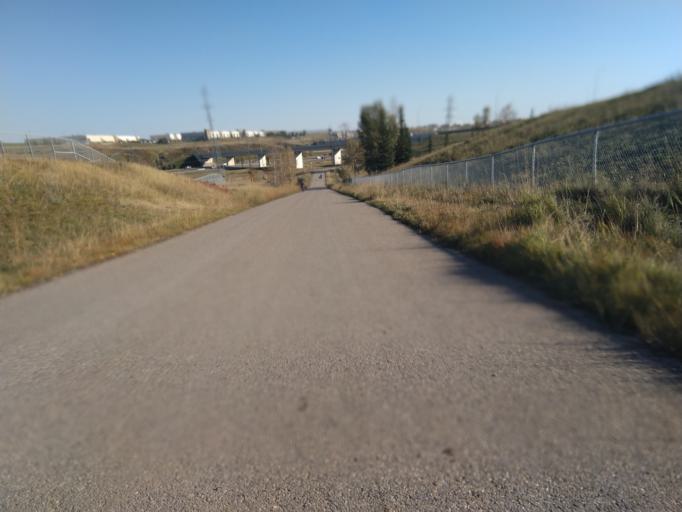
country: CA
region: Alberta
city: Calgary
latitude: 51.1281
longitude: -114.0505
